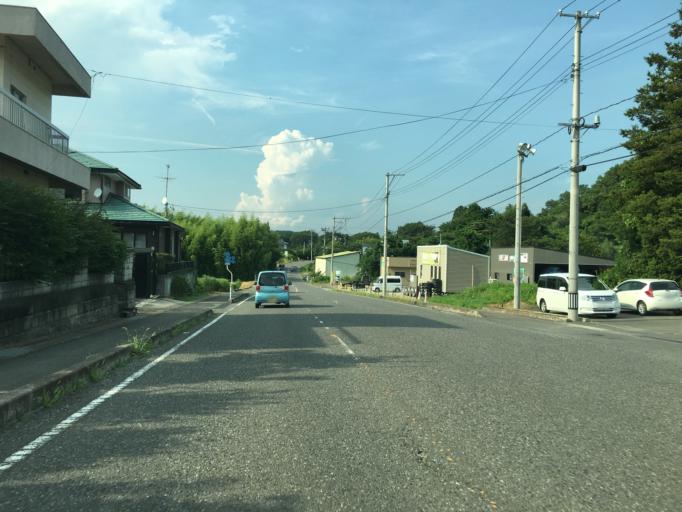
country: JP
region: Fukushima
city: Miharu
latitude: 37.4476
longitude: 140.4275
